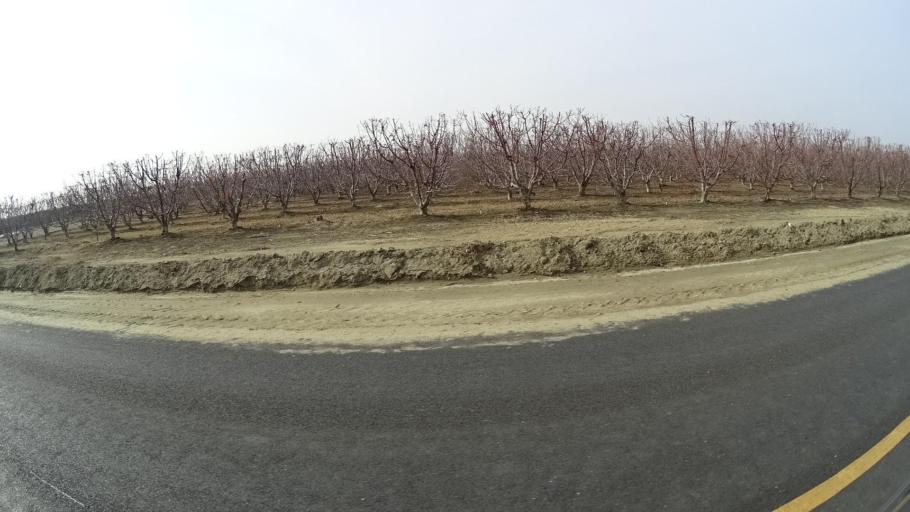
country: US
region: California
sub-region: Kern County
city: Arvin
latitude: 35.1594
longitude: -118.8509
